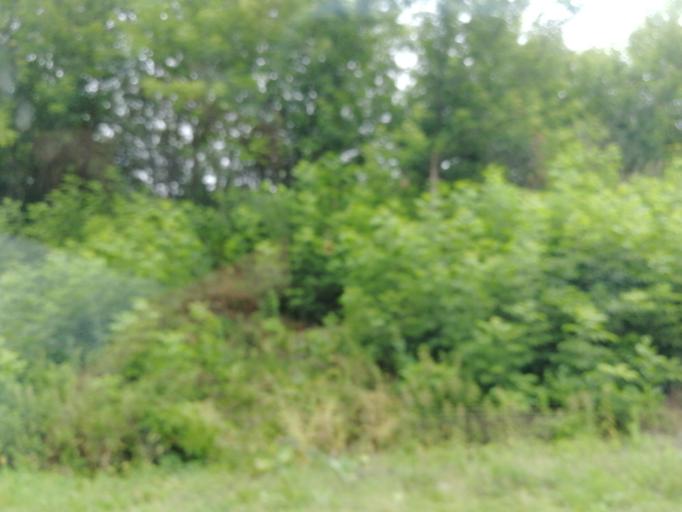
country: RU
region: Tula
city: Tovarkovskiy
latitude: 53.6933
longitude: 38.1693
